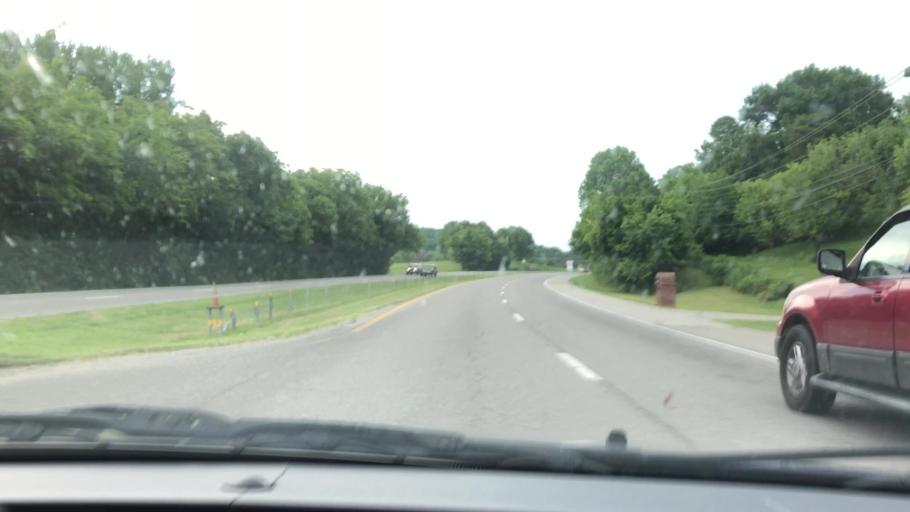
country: US
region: Tennessee
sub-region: Maury County
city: Columbia
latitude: 35.6761
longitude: -86.9998
